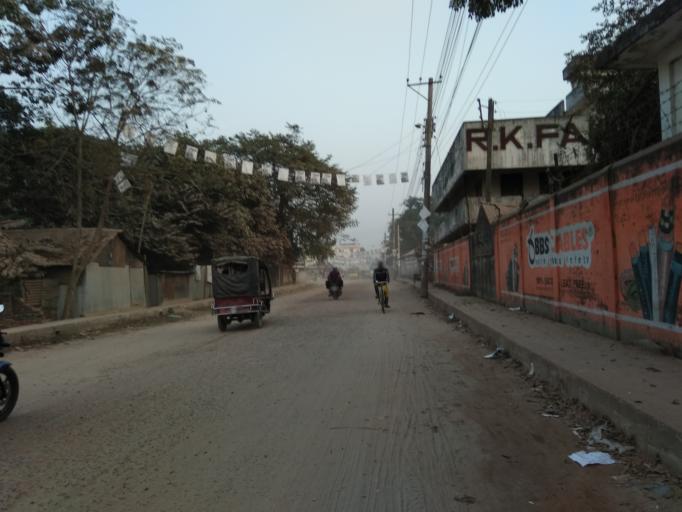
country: BD
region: Rangpur Division
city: Rangpur
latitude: 25.7322
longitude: 89.2631
